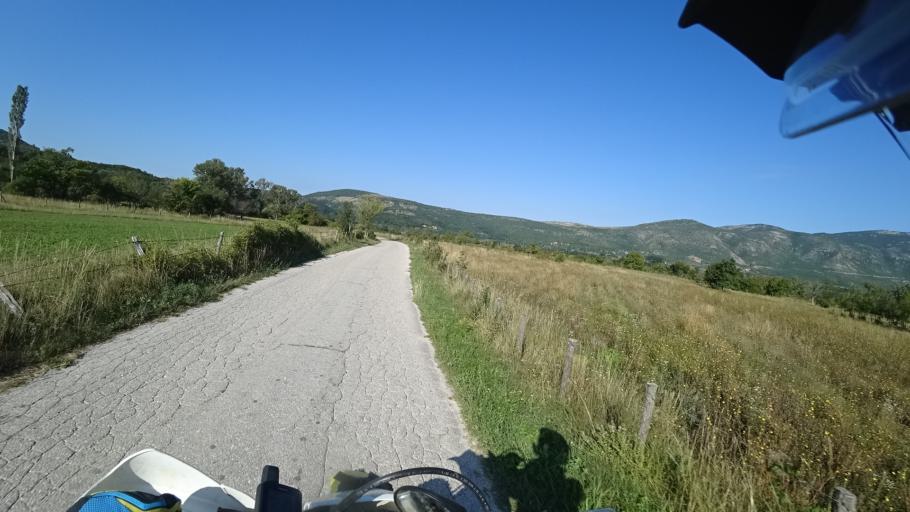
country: HR
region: Sibensko-Kniniska
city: Knin
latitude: 44.1499
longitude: 16.1761
